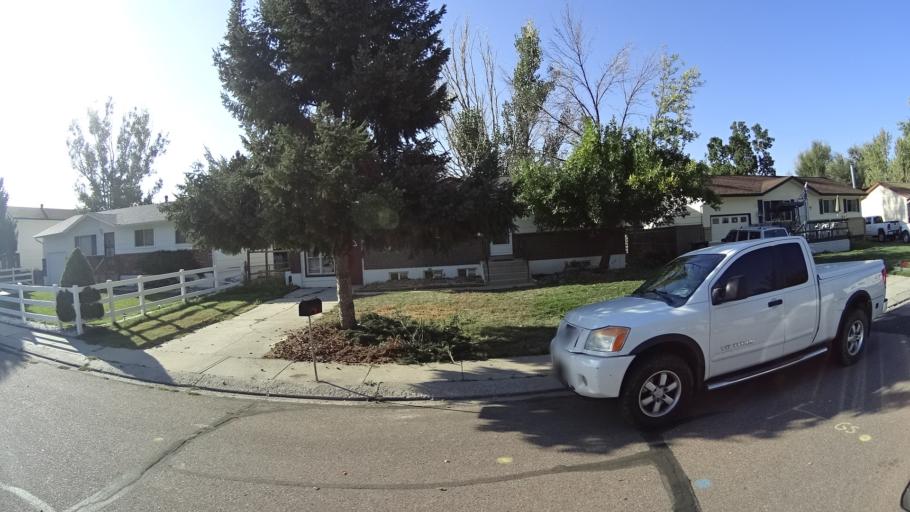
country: US
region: Colorado
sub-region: El Paso County
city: Cimarron Hills
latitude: 38.8909
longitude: -104.7455
